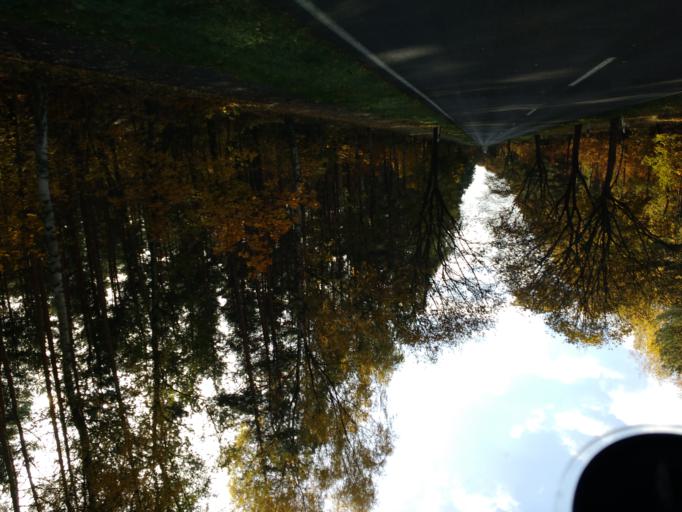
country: DE
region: Brandenburg
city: Grunheide
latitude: 52.3794
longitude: 13.8321
